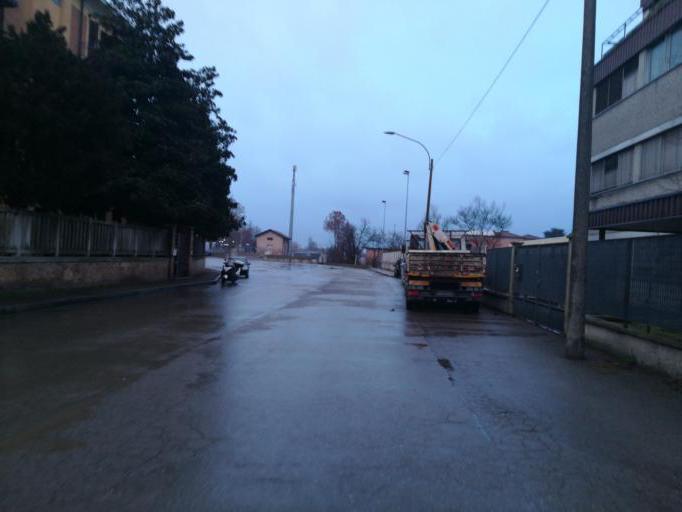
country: IT
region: Emilia-Romagna
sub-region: Provincia di Bologna
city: Progresso
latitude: 44.5510
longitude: 11.3544
